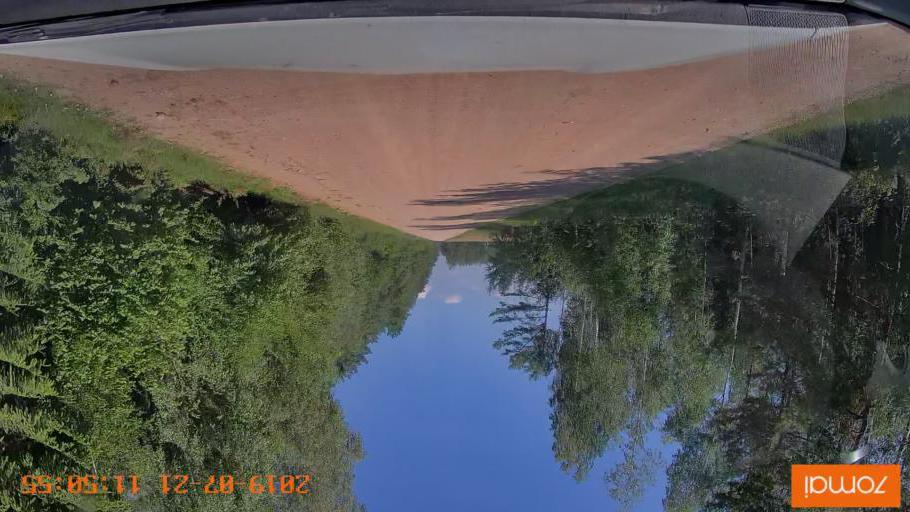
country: BY
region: Grodnenskaya
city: Lyubcha
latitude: 53.8850
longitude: 26.0184
